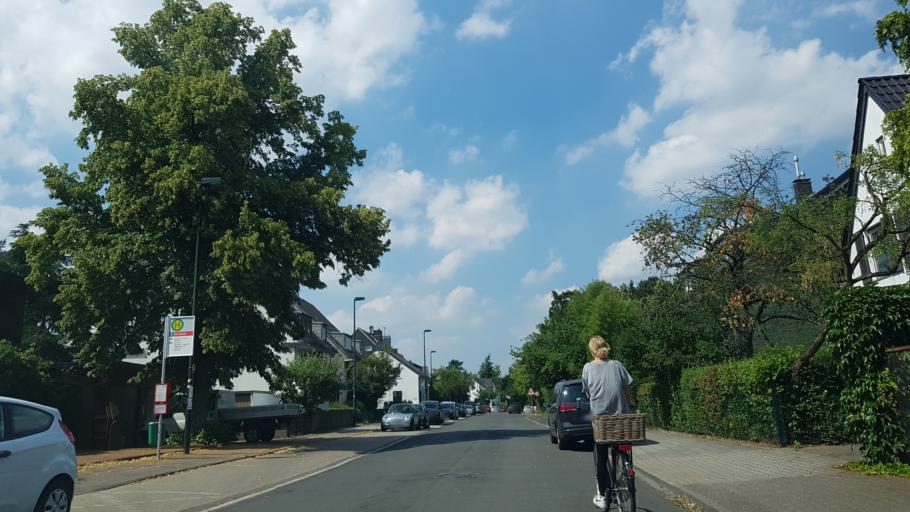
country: DE
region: North Rhine-Westphalia
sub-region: Regierungsbezirk Dusseldorf
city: Meerbusch
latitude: 51.2770
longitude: 6.7369
